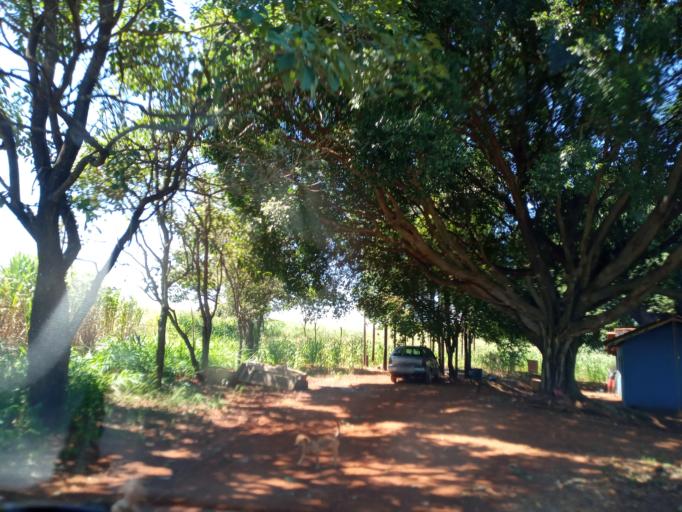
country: BR
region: Goias
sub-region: Itumbiara
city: Itumbiara
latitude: -18.4409
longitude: -49.1320
